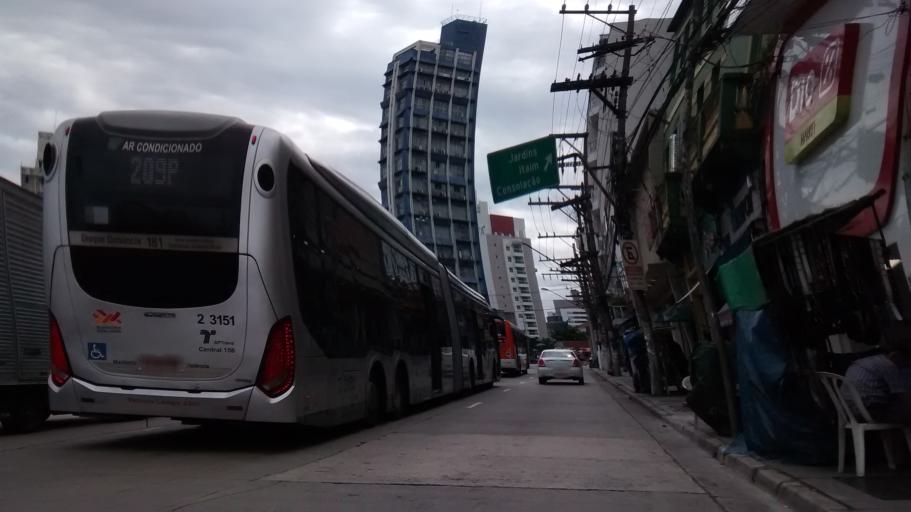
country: BR
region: Sao Paulo
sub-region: Sao Paulo
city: Sao Paulo
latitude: -23.5671
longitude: -46.6946
